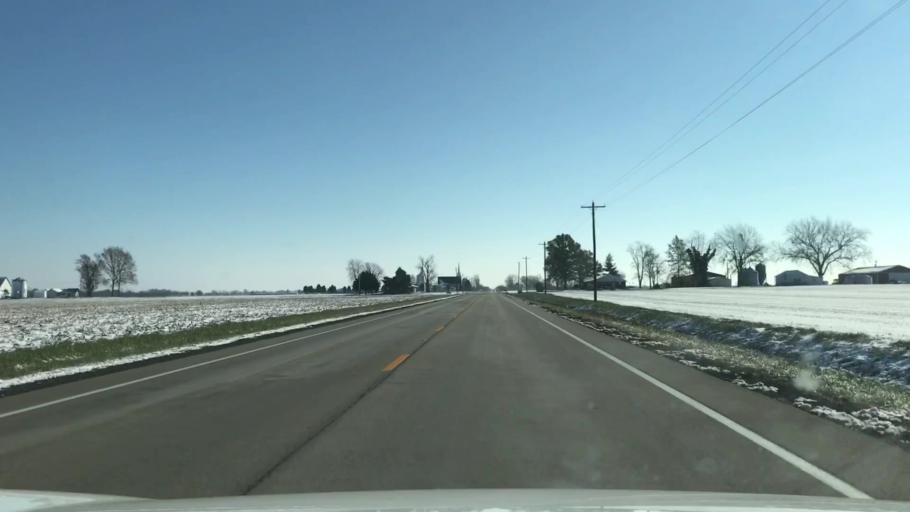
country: US
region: Illinois
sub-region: Washington County
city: Okawville
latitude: 38.4423
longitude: -89.4997
